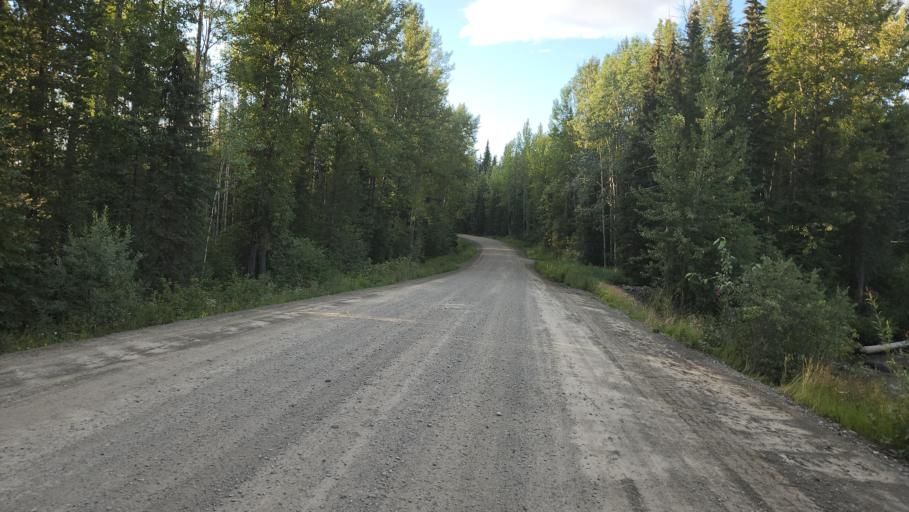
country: CA
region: British Columbia
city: Quesnel
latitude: 53.0180
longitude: -122.0820
